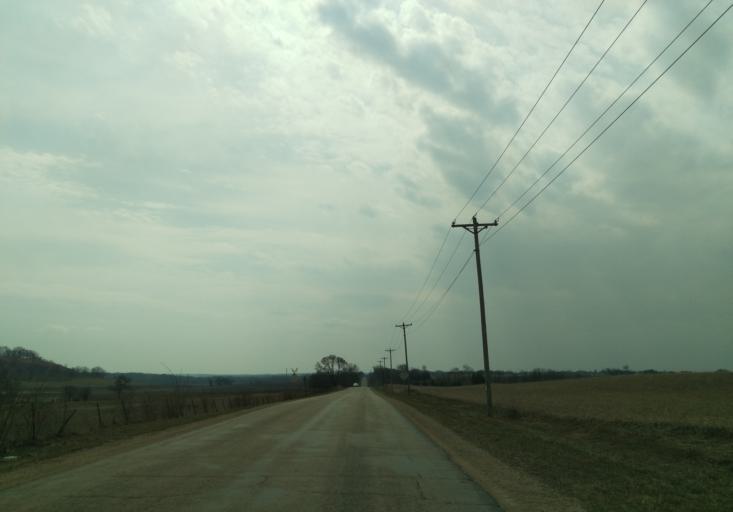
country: US
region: Wisconsin
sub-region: Dane County
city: Middleton
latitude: 43.1325
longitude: -89.4916
